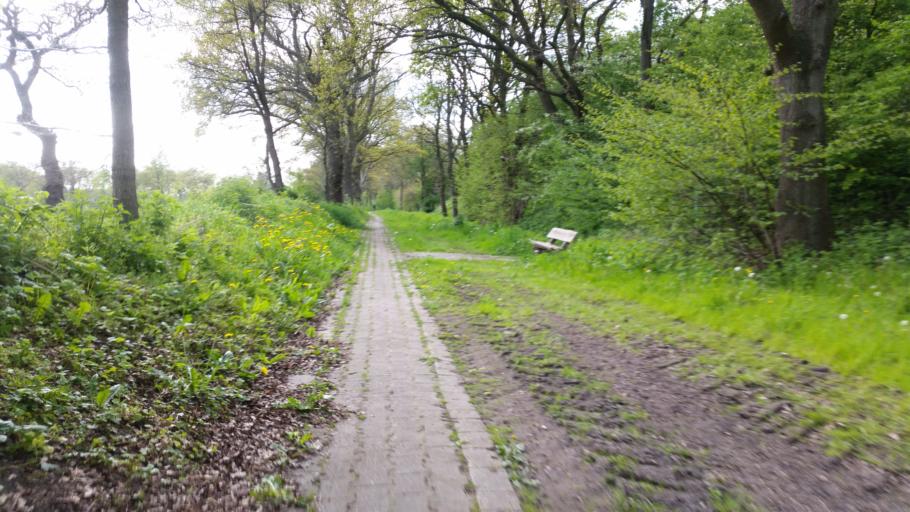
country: DE
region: Lower Saxony
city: Aurich
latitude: 53.4545
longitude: 7.4944
